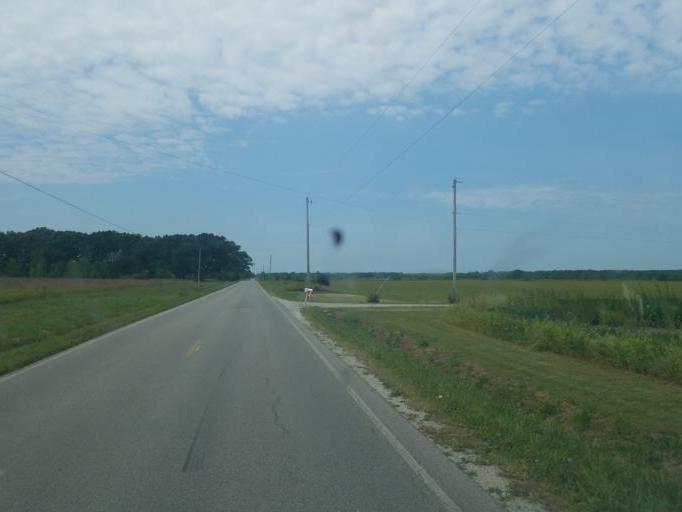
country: US
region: Ohio
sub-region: Marion County
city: Marion
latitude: 40.5713
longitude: -83.1735
